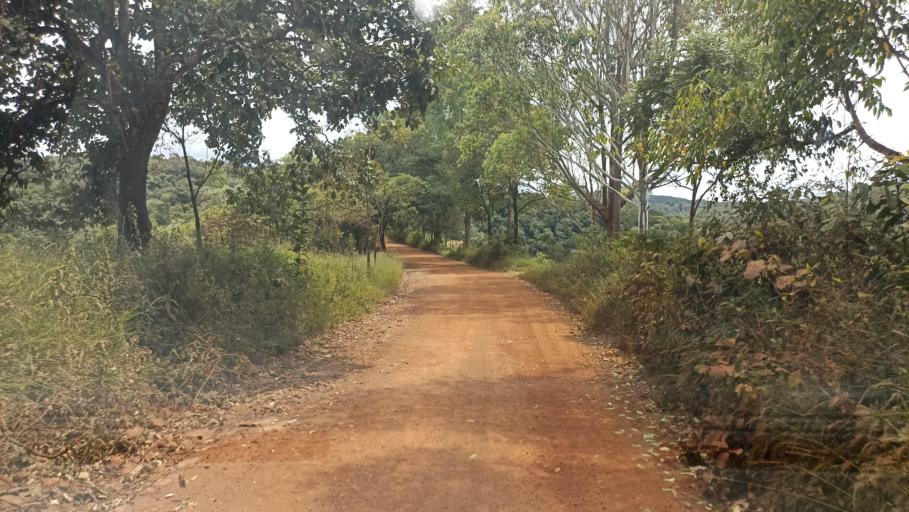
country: BR
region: Minas Gerais
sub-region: Itabirito
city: Itabirito
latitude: -20.3529
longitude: -43.7379
